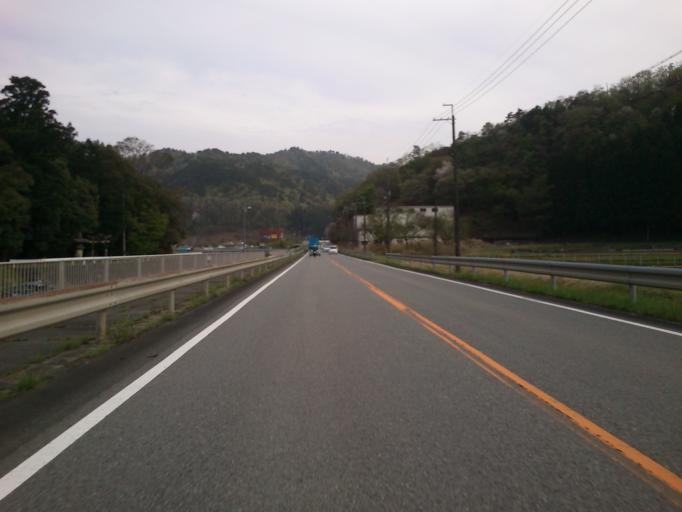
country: JP
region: Hyogo
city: Sasayama
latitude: 35.1224
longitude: 135.3365
